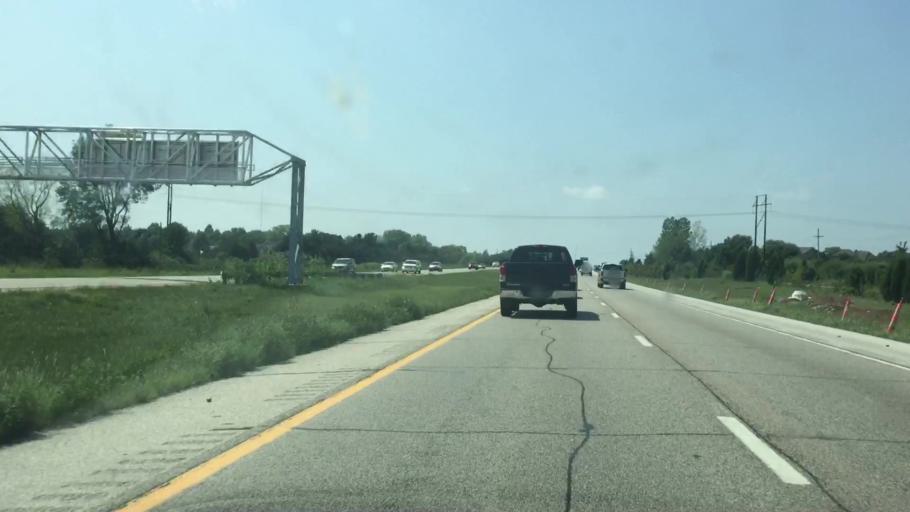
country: US
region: Kansas
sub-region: Johnson County
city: Olathe
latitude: 38.9412
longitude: -94.8263
